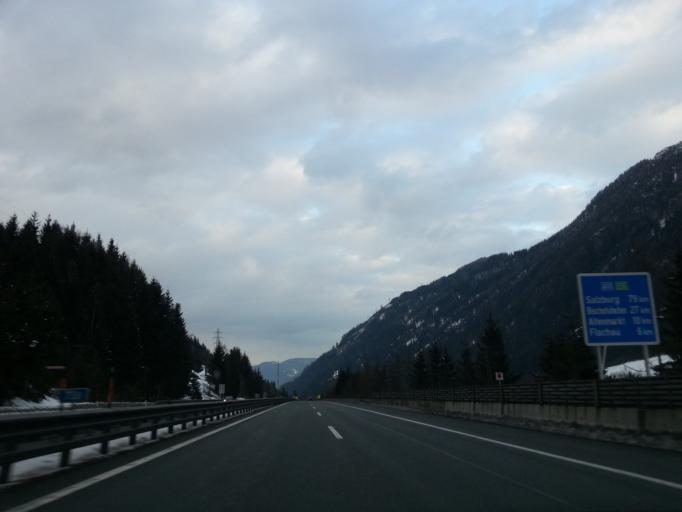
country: AT
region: Salzburg
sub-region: Politischer Bezirk Sankt Johann im Pongau
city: Flachau
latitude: 47.3032
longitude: 13.3925
